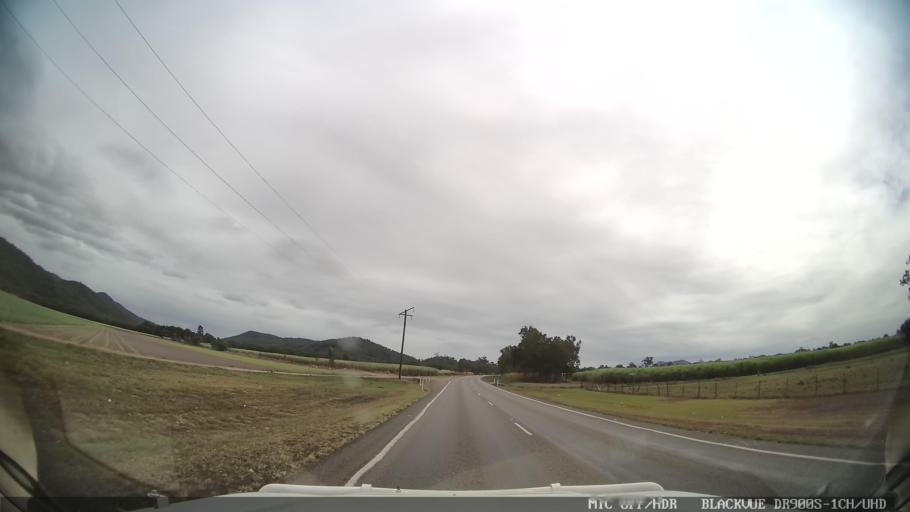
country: AU
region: Queensland
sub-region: Hinchinbrook
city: Ingham
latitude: -18.8559
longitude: 146.1636
